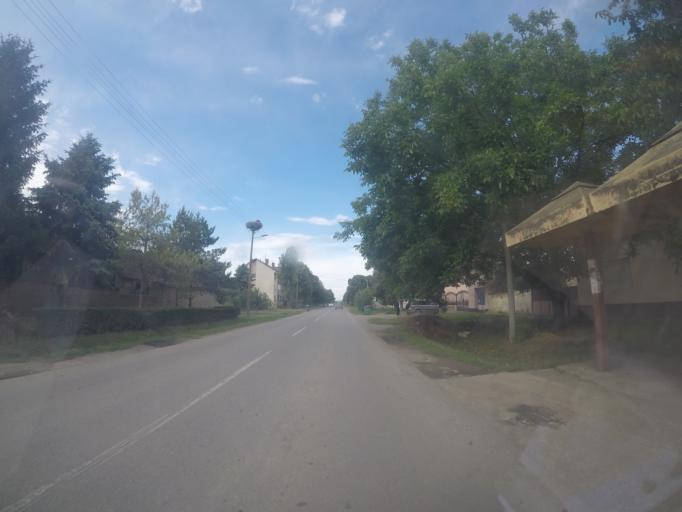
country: RS
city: Perlez
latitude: 45.2118
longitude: 20.3788
